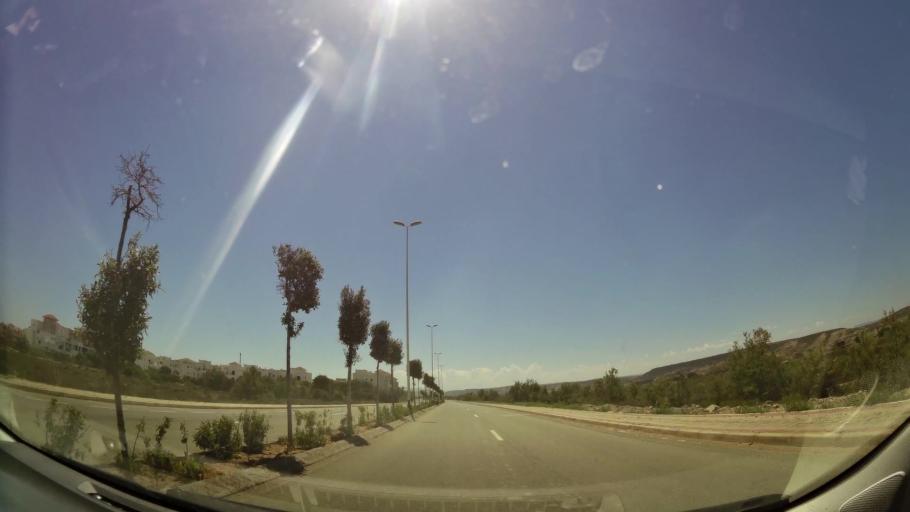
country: MA
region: Oriental
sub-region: Berkane-Taourirt
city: Madagh
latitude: 35.1007
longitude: -2.3093
